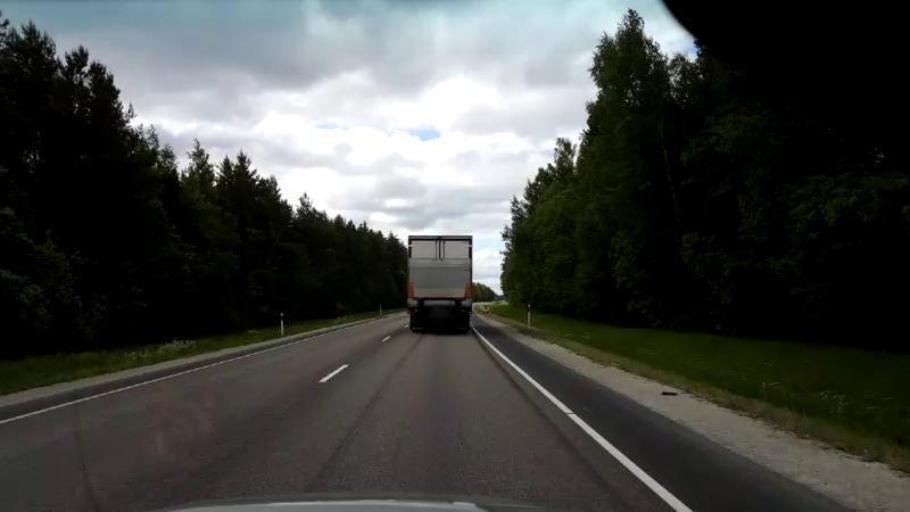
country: EE
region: Raplamaa
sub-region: Maerjamaa vald
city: Marjamaa
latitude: 58.7551
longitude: 24.4232
